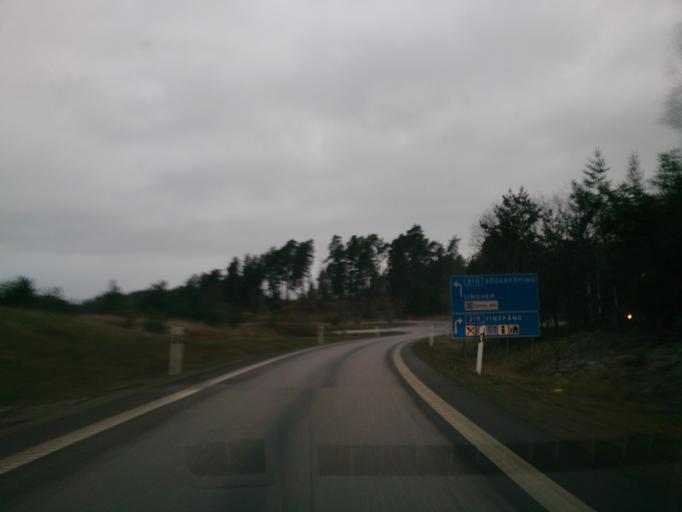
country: SE
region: OEstergoetland
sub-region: Norrkopings Kommun
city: Kimstad
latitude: 58.4903
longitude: 15.9517
